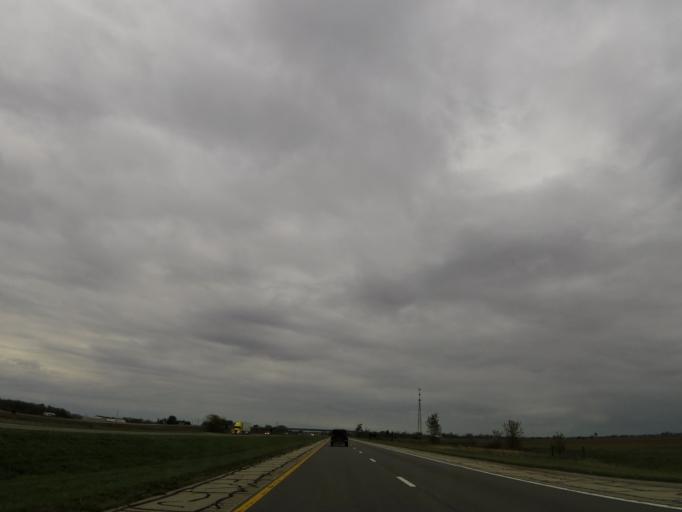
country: US
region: Ohio
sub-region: Madison County
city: Bethel
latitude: 39.7280
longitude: -83.3799
